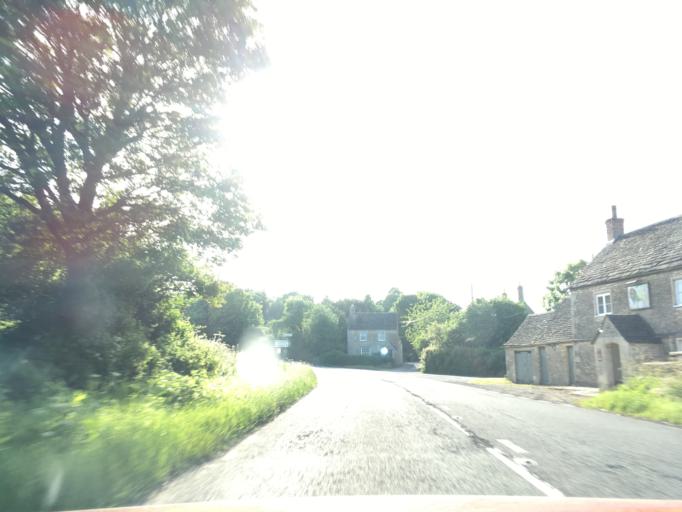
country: GB
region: England
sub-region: Wiltshire
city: Cricklade
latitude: 51.7110
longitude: -1.8724
